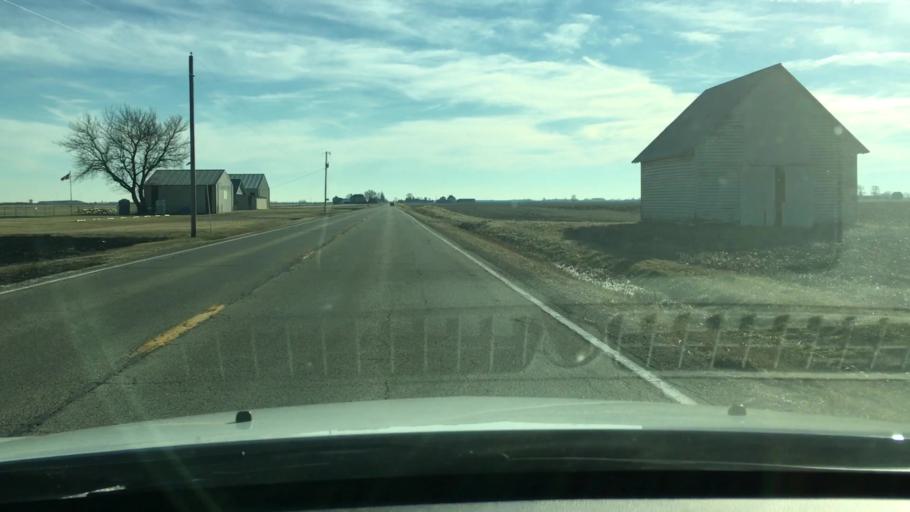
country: US
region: Illinois
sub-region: LaSalle County
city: Peru
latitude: 41.4215
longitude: -89.1264
